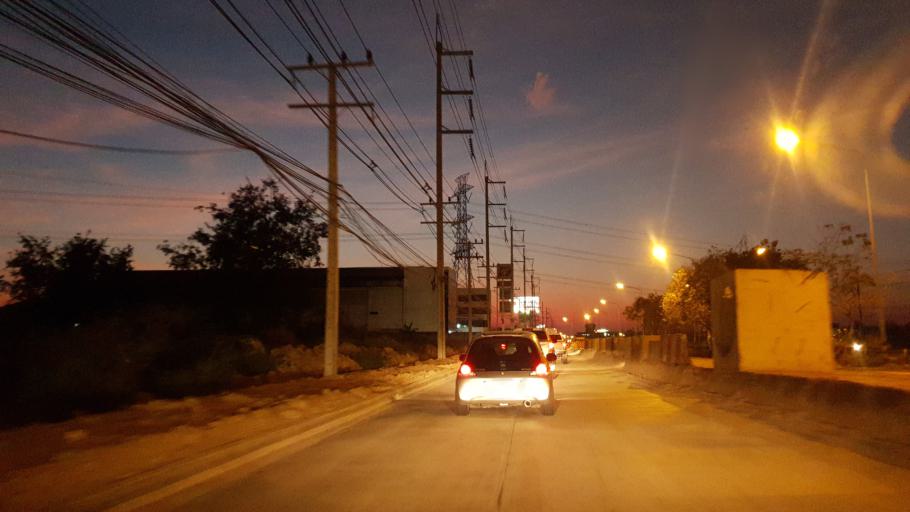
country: TH
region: Phitsanulok
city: Phitsanulok
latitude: 16.8181
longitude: 100.3383
